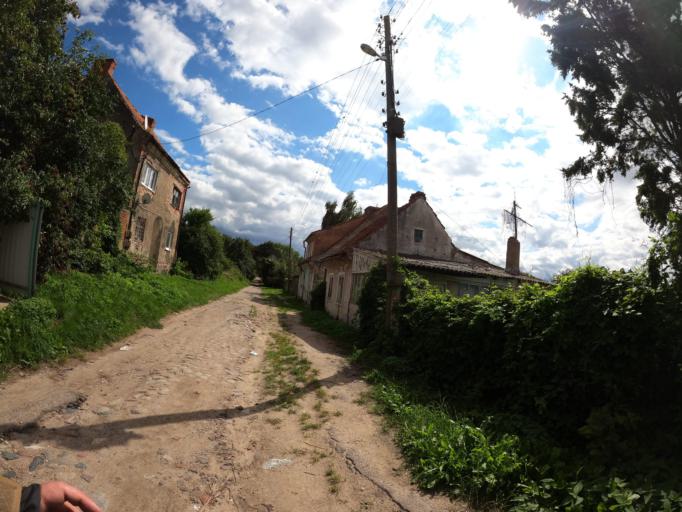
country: RU
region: Kaliningrad
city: Zheleznodorozhnyy
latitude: 54.3605
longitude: 21.3042
